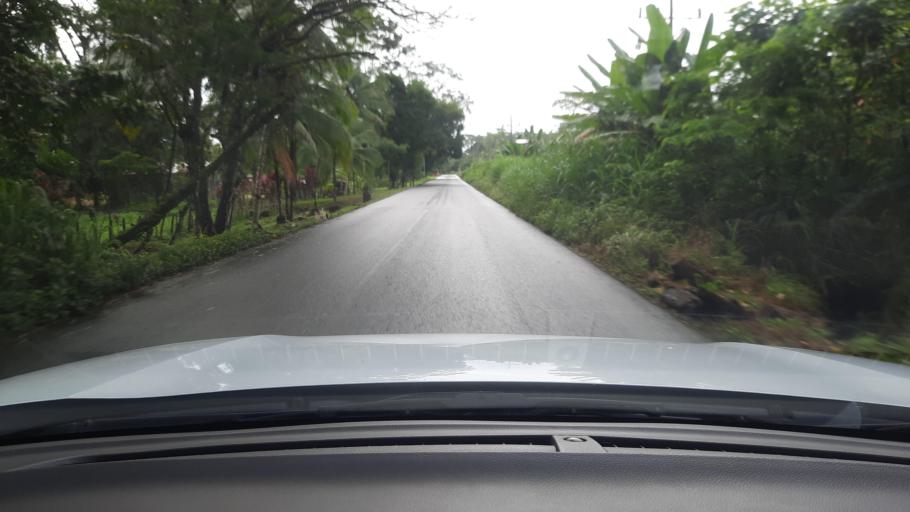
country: CR
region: Alajuela
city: Upala
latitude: 10.9256
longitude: -85.0741
